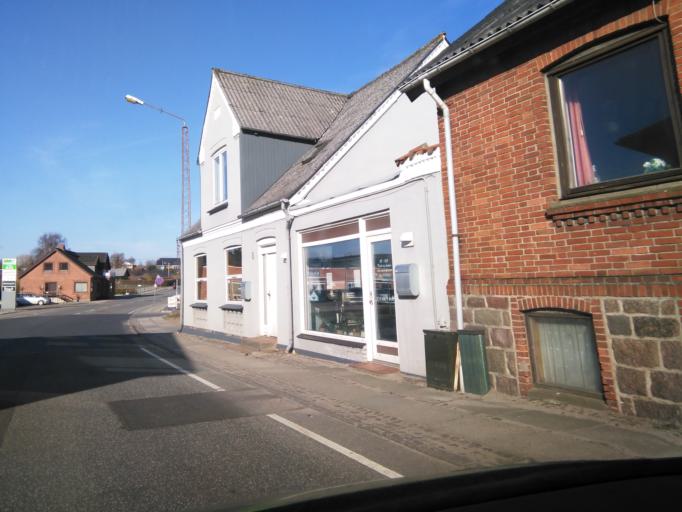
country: DK
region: Central Jutland
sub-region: Skanderborg Kommune
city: Ry
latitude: 55.9682
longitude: 9.7492
